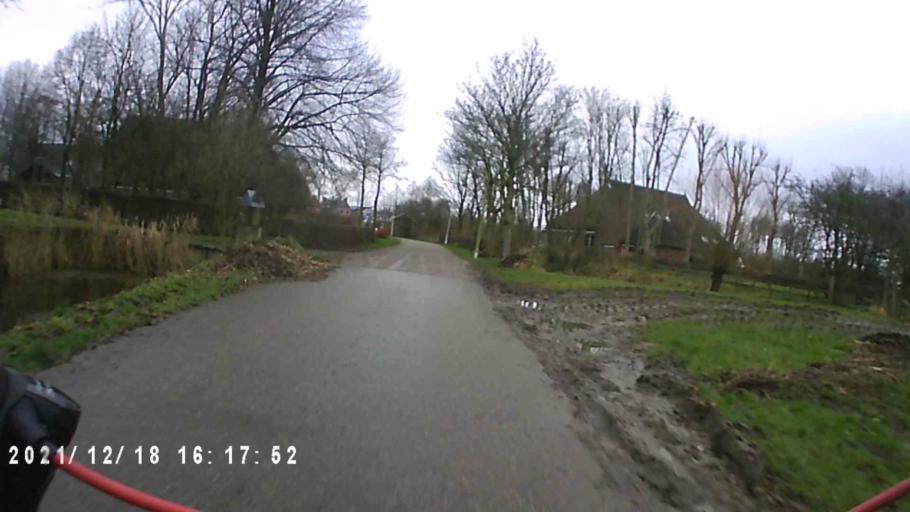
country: NL
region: Friesland
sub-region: Gemeente Dongeradeel
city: Anjum
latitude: 53.3761
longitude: 6.0573
